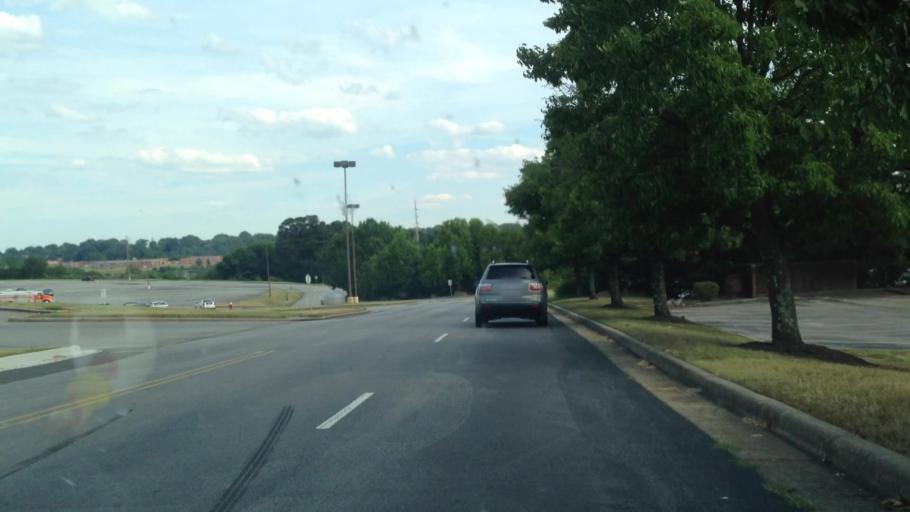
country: US
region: Virginia
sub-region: City of Danville
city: Danville
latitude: 36.5937
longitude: -79.4246
